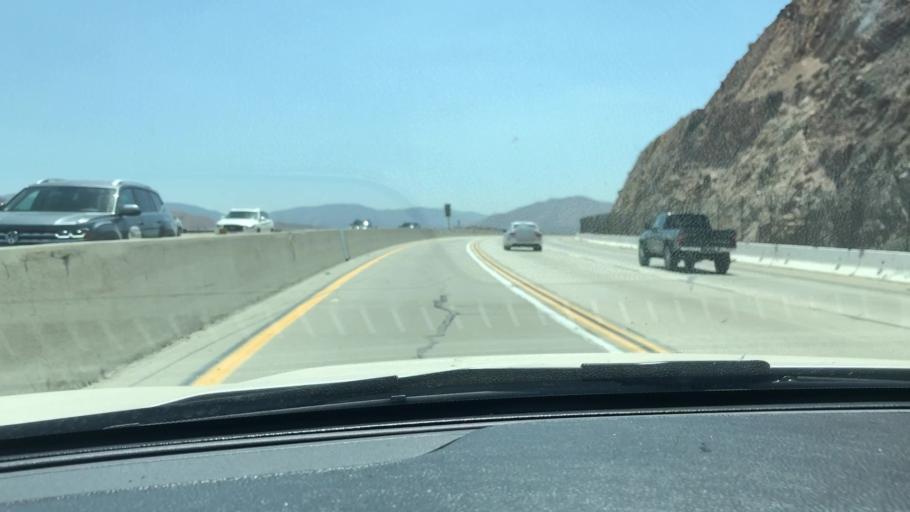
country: US
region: California
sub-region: Los Angeles County
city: Vincent
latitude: 34.4925
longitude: -118.1283
